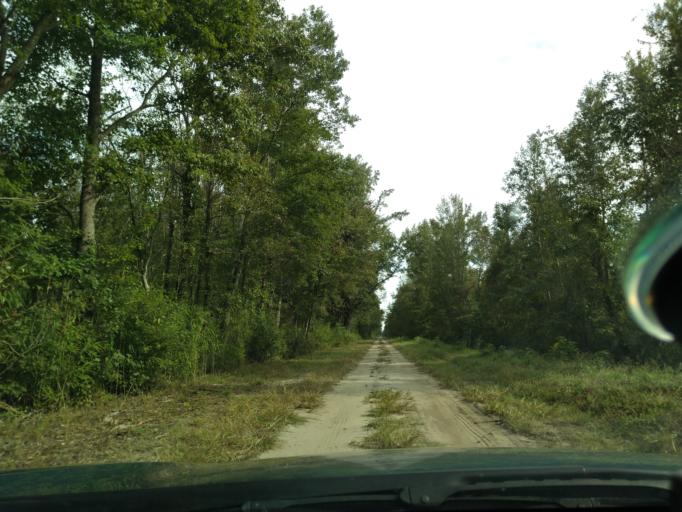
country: US
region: North Carolina
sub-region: Beaufort County
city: Belhaven
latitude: 35.7053
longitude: -76.5717
